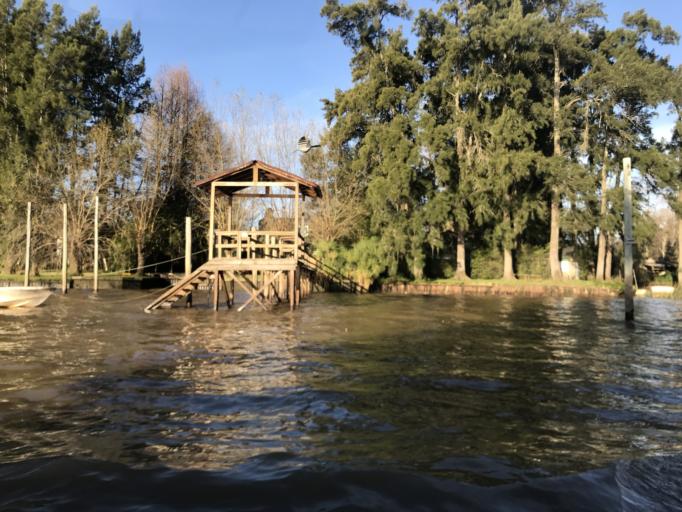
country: AR
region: Buenos Aires
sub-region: Partido de Tigre
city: Tigre
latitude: -34.3990
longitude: -58.5944
